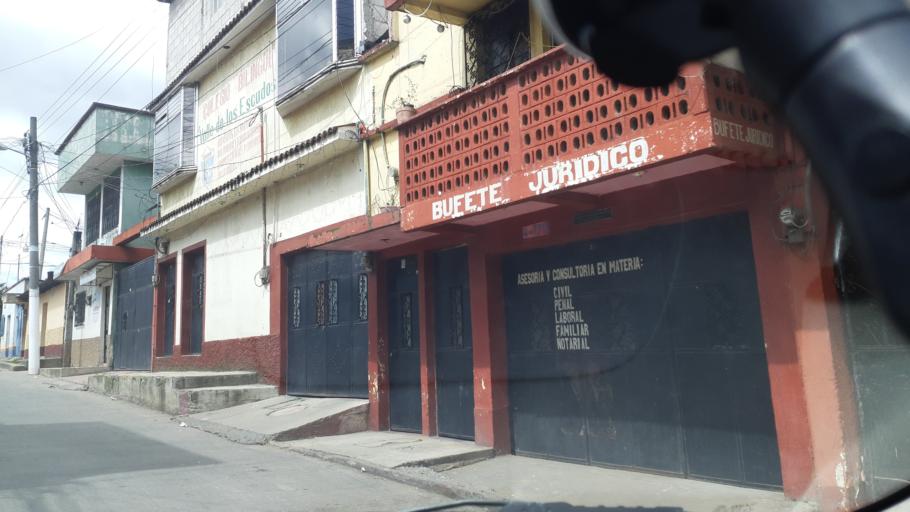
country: GT
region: Chimaltenango
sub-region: Municipio de Chimaltenango
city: Chimaltenango
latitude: 14.6640
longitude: -90.8238
